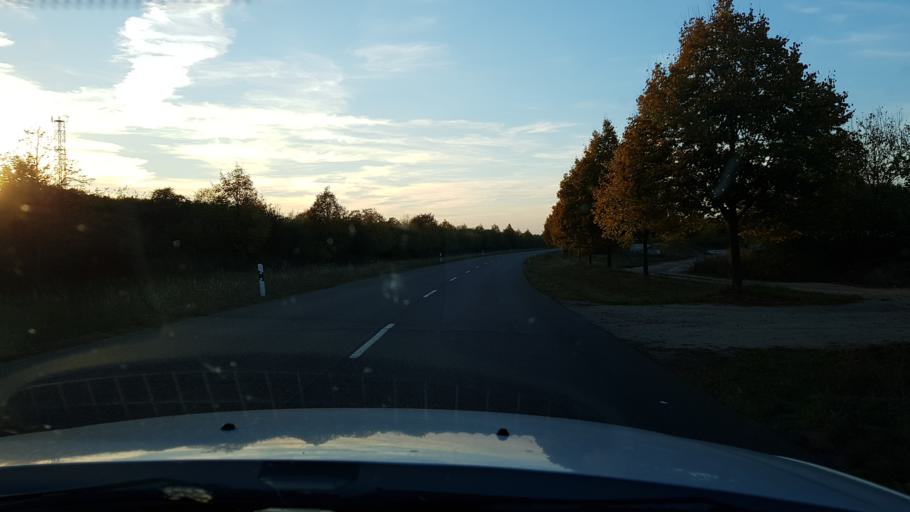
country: DE
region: Brandenburg
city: Schwedt (Oder)
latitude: 53.1011
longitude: 14.3178
